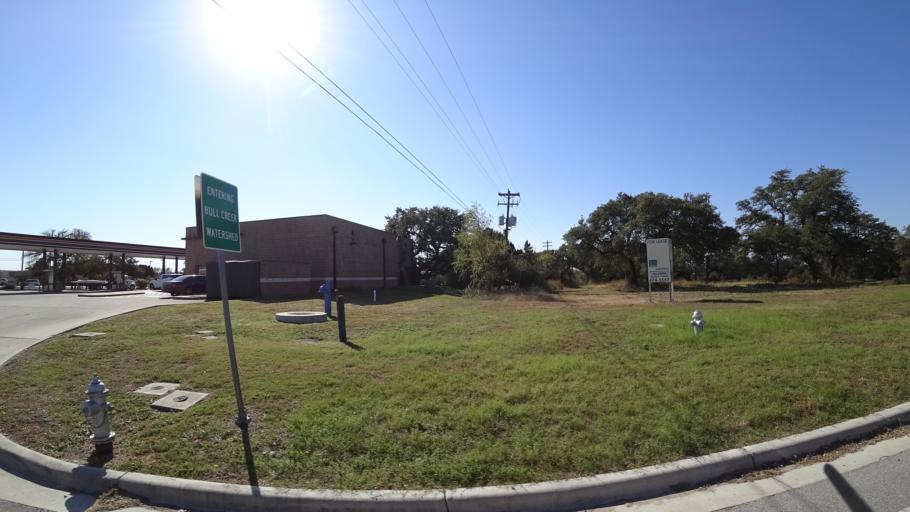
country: US
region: Texas
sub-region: Williamson County
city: Anderson Mill
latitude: 30.4557
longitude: -97.8274
